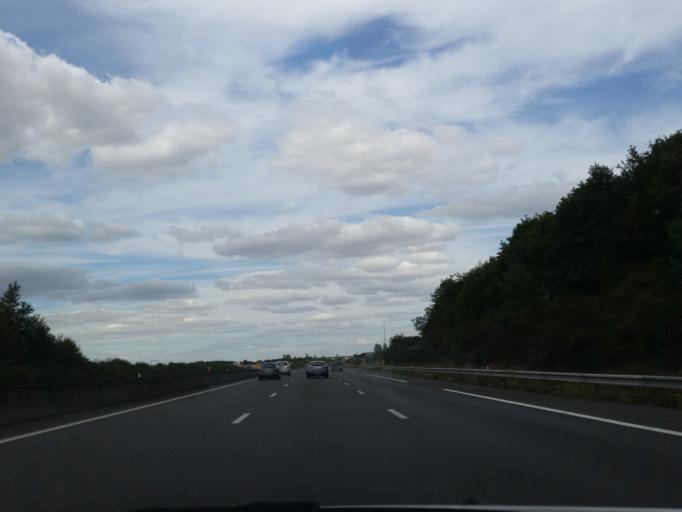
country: FR
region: Centre
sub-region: Departement du Loir-et-Cher
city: Herbault
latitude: 47.5753
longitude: 1.0579
